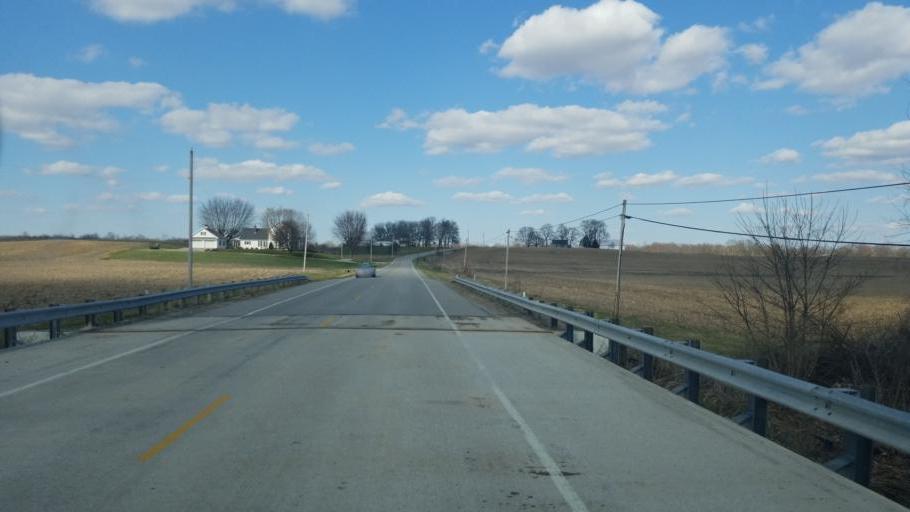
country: US
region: Ohio
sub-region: Highland County
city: Greenfield
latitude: 39.3371
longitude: -83.4045
